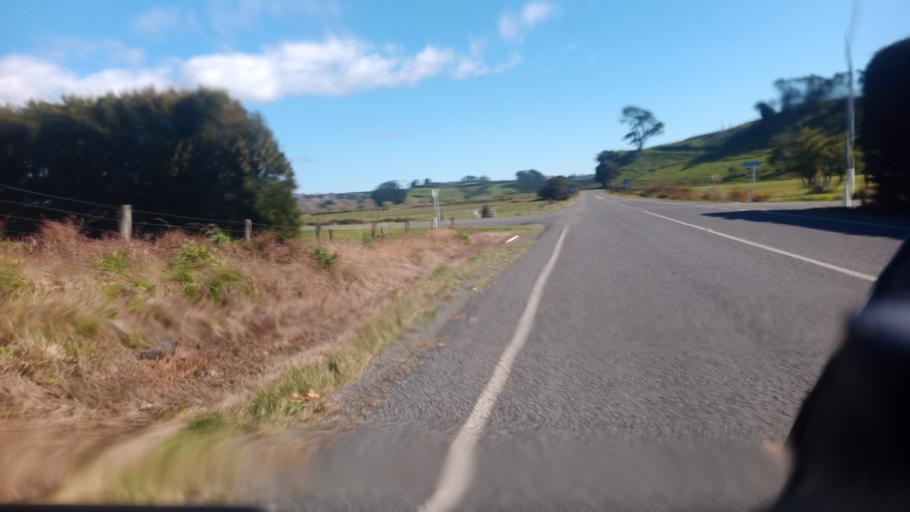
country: NZ
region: Bay of Plenty
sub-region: Opotiki District
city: Opotiki
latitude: -37.9896
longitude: 177.3497
